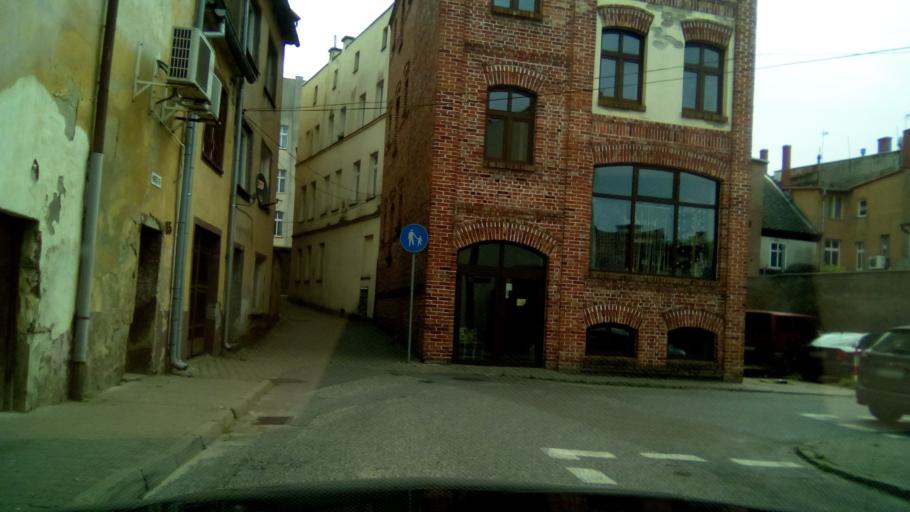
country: PL
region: Pomeranian Voivodeship
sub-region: Powiat chojnicki
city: Chojnice
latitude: 53.6944
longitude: 17.5629
